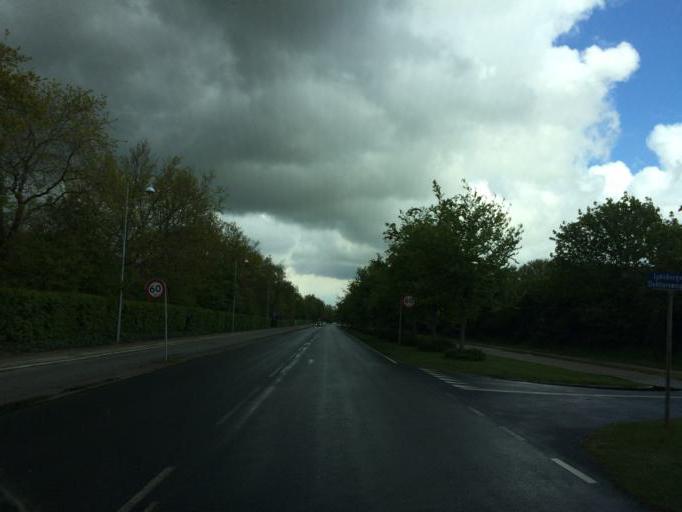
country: DK
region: Central Jutland
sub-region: Holstebro Kommune
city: Holstebro
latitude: 56.3705
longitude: 8.6110
